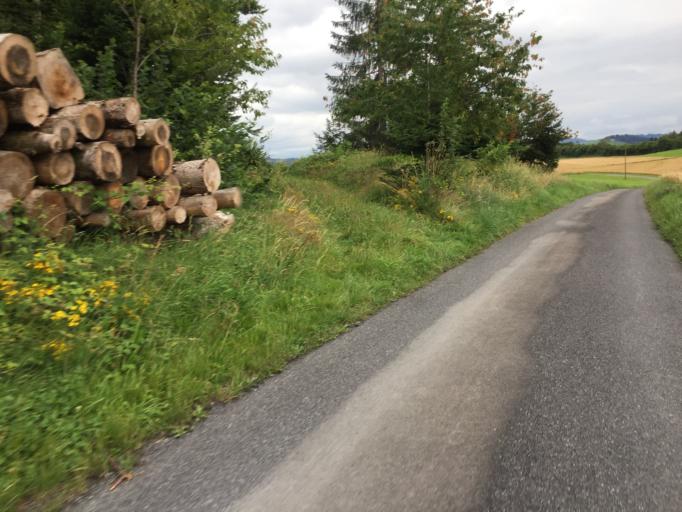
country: CH
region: Bern
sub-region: Bern-Mittelland District
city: Stettlen
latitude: 46.9422
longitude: 7.5270
